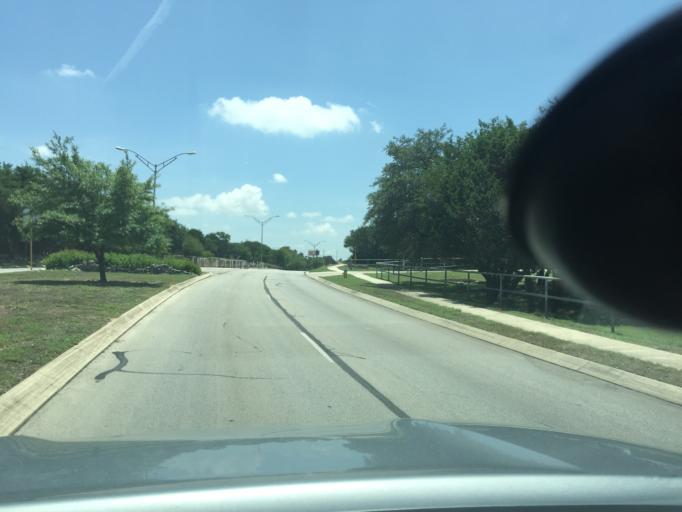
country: US
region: Texas
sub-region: Bexar County
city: Timberwood Park
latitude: 29.6850
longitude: -98.4596
